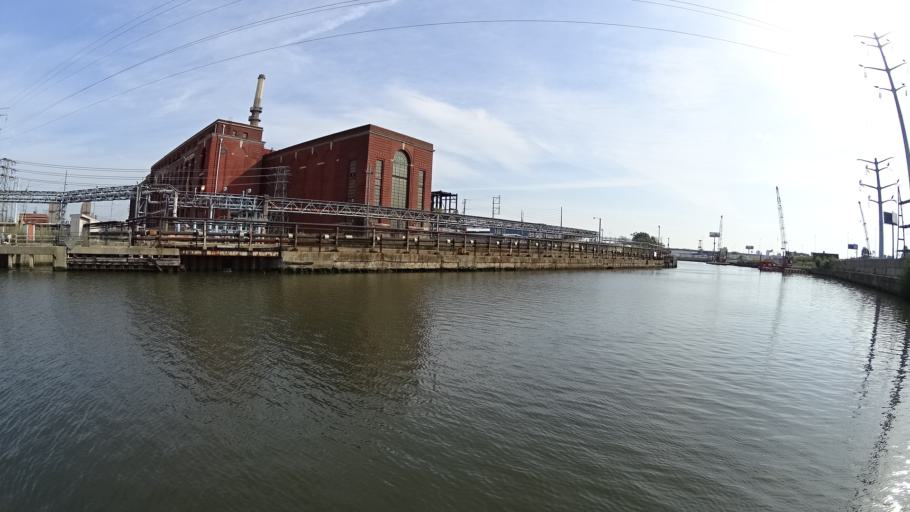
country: US
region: Illinois
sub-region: Cook County
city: Chicago
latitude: 41.8473
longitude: -87.6546
